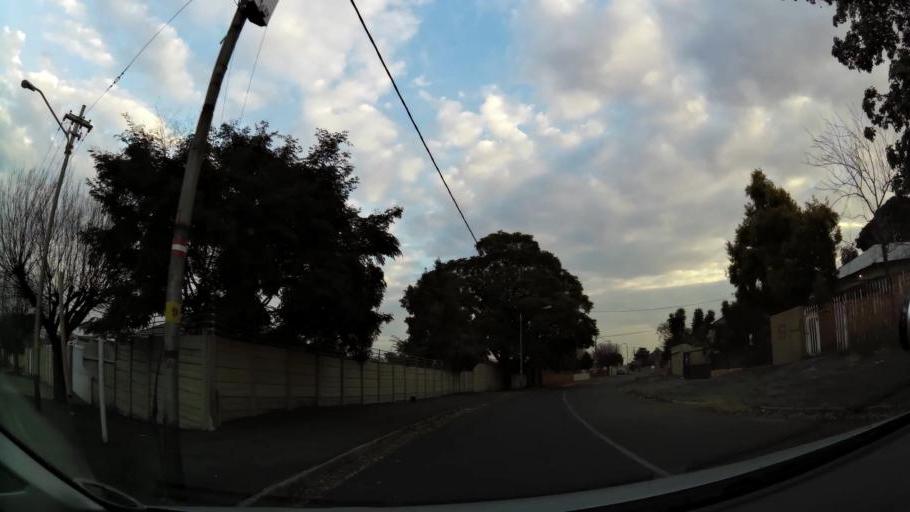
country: ZA
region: Gauteng
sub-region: Ekurhuleni Metropolitan Municipality
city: Germiston
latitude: -26.1890
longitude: 28.1523
